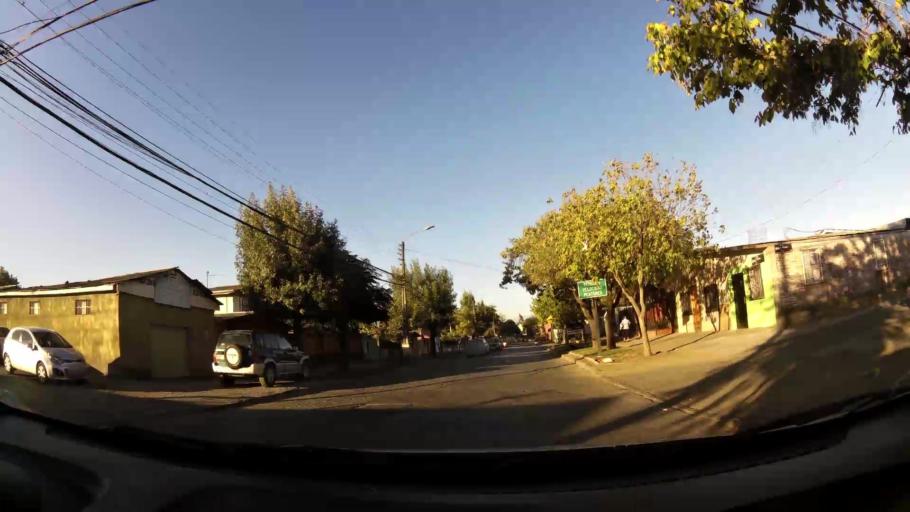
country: CL
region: O'Higgins
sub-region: Provincia de Cachapoal
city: Rancagua
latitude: -34.1697
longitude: -70.7612
